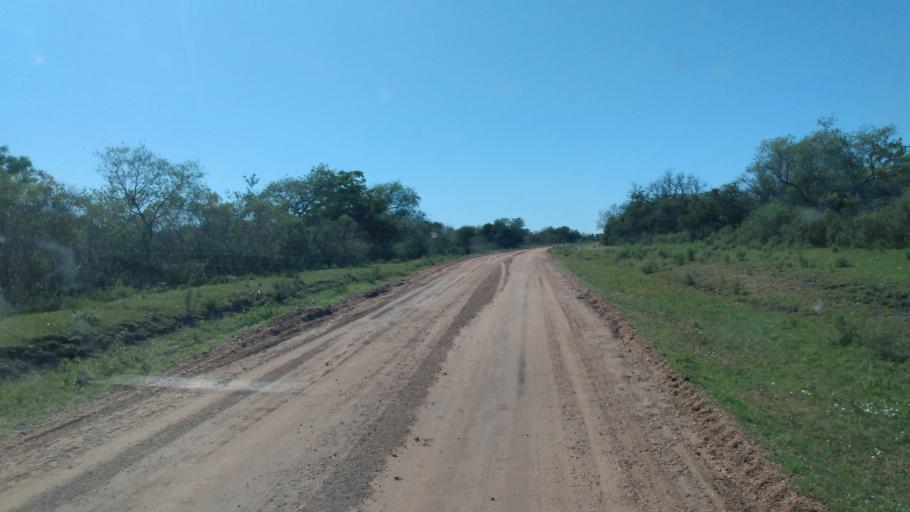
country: AR
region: Entre Rios
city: Ubajay
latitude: -31.8697
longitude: -58.2434
